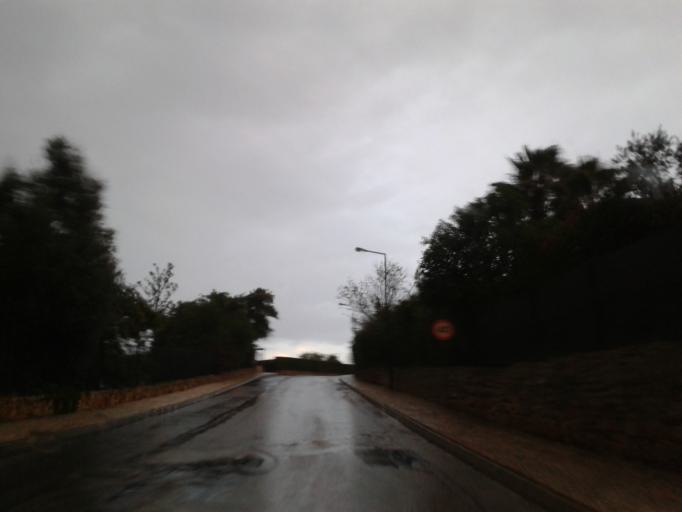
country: PT
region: Faro
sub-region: Lagoa
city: Estombar
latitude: 37.1305
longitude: -8.4857
